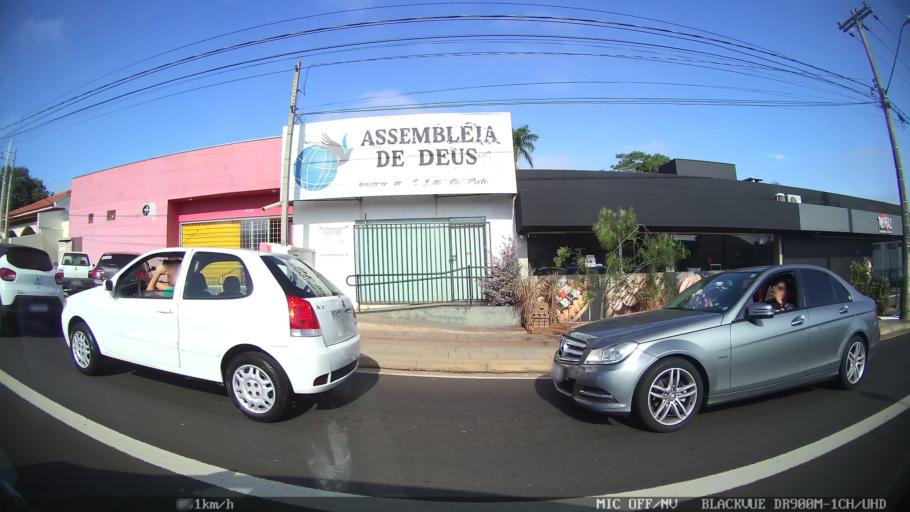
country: BR
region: Sao Paulo
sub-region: Sao Jose Do Rio Preto
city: Sao Jose do Rio Preto
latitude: -20.8082
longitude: -49.4006
